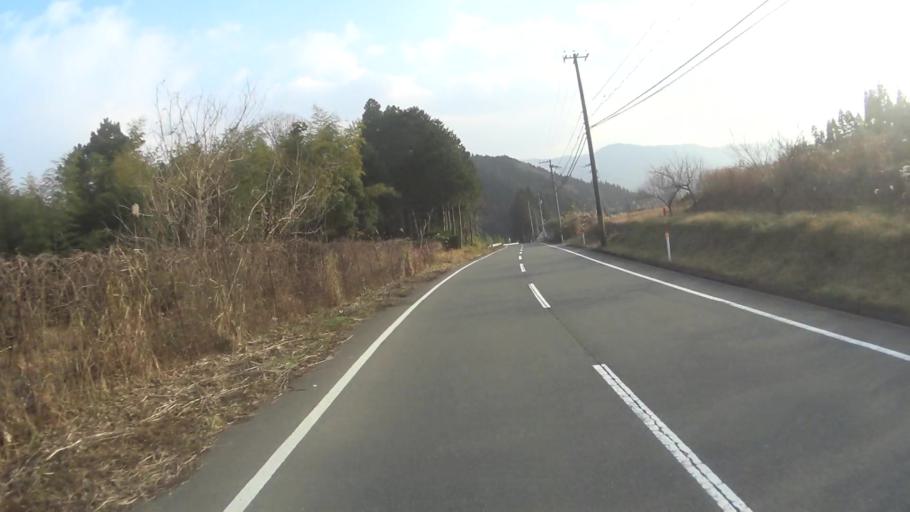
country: JP
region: Kyoto
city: Maizuru
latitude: 35.3816
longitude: 135.4187
